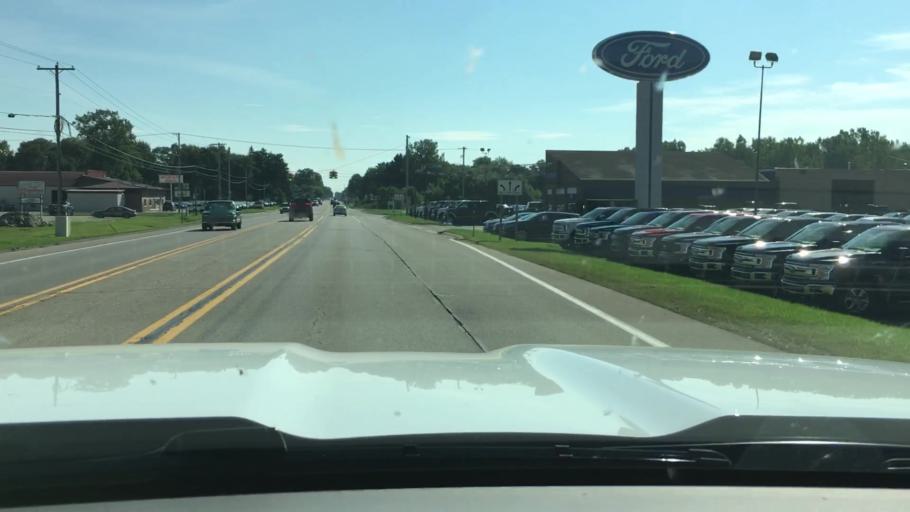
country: US
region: Michigan
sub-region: Gratiot County
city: Alma
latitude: 43.4079
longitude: -84.6483
